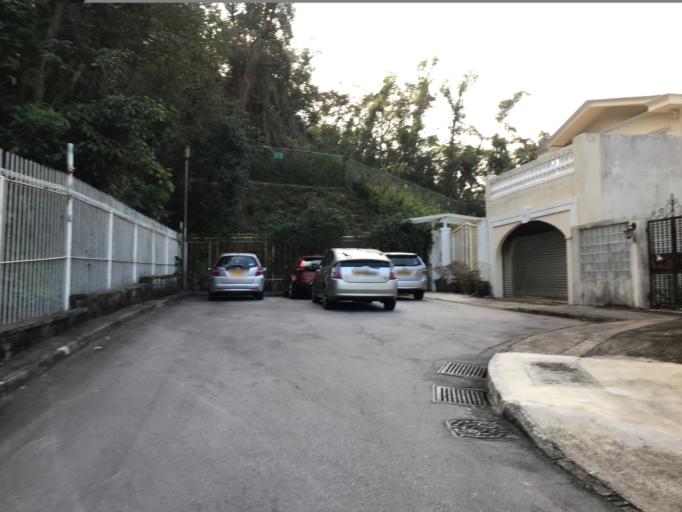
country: HK
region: Tai Po
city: Tai Po
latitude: 22.4605
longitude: 114.1569
